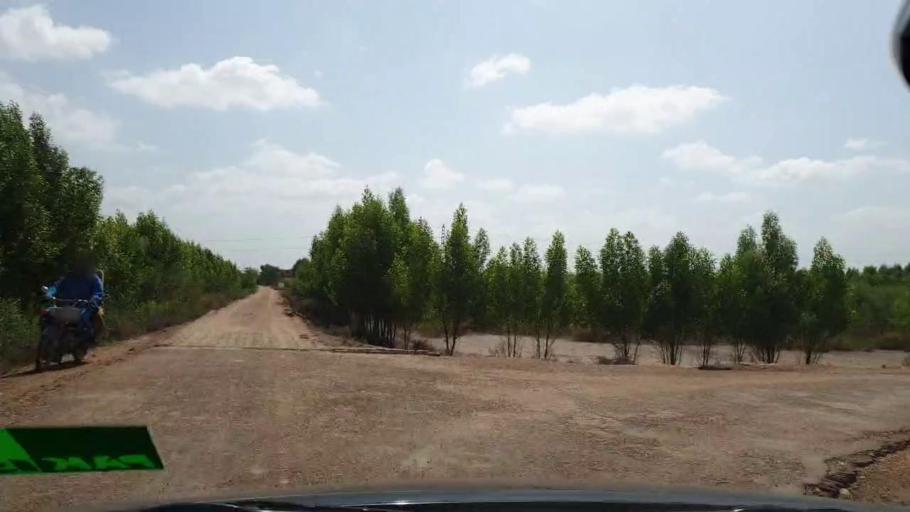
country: PK
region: Sindh
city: Kadhan
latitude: 24.6177
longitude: 69.1842
